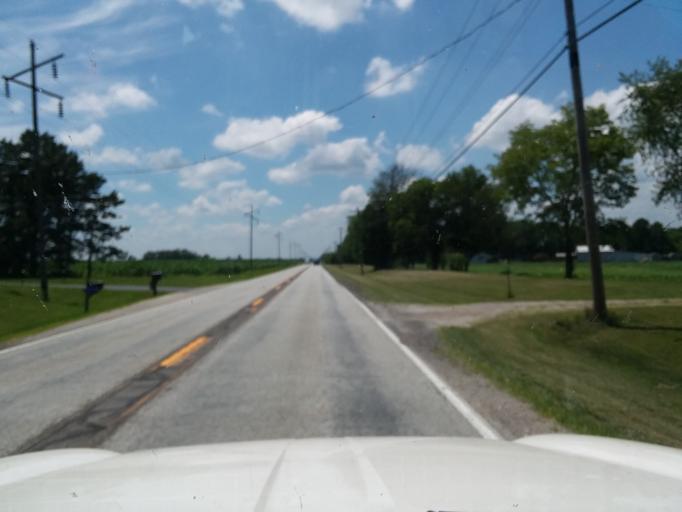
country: US
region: Indiana
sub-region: Johnson County
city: Trafalgar
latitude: 39.3981
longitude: -86.2005
